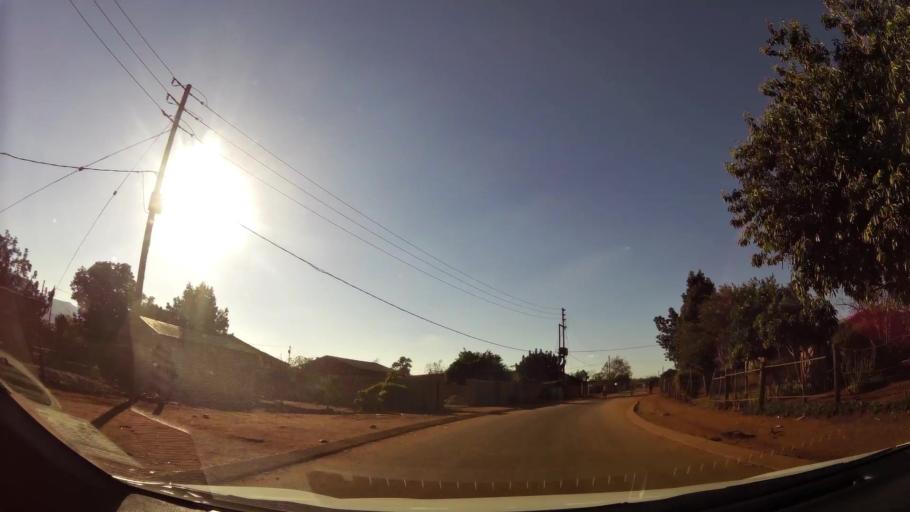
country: ZA
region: Limpopo
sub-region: Waterberg District Municipality
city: Mokopane
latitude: -24.1819
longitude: 28.9775
